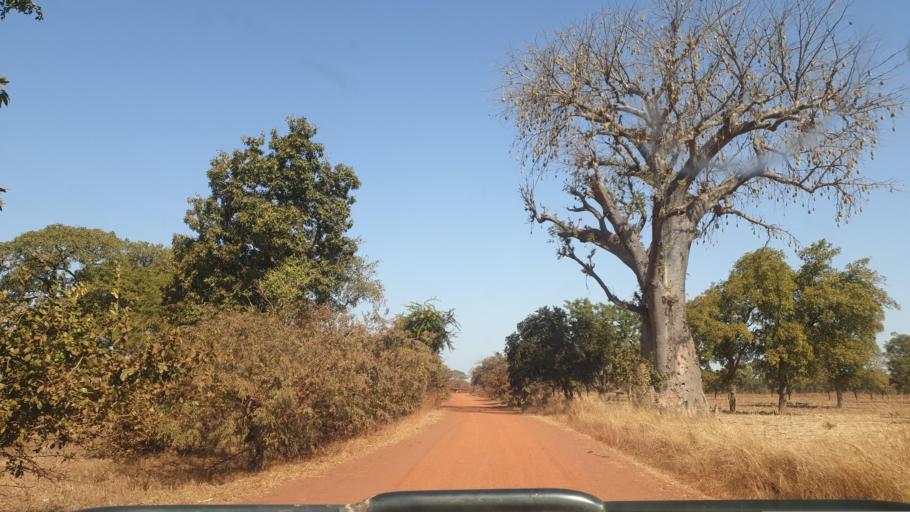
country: ML
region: Sikasso
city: Bougouni
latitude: 11.8445
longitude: -6.9783
